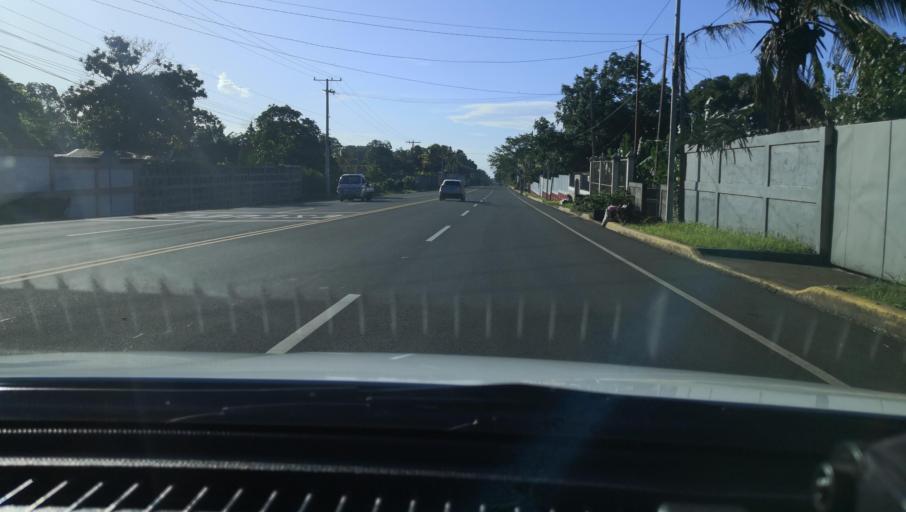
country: NI
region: Carazo
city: Jinotepe
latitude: 11.8272
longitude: -86.1712
